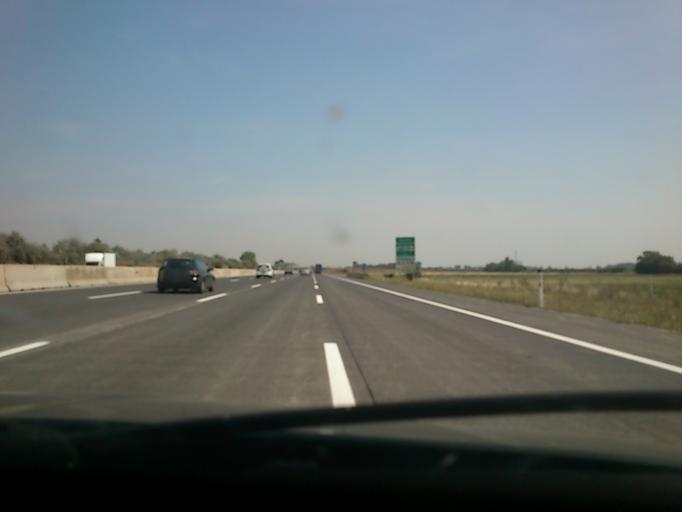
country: AT
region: Lower Austria
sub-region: Politischer Bezirk Baden
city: Traiskirchen
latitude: 48.0082
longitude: 16.3120
